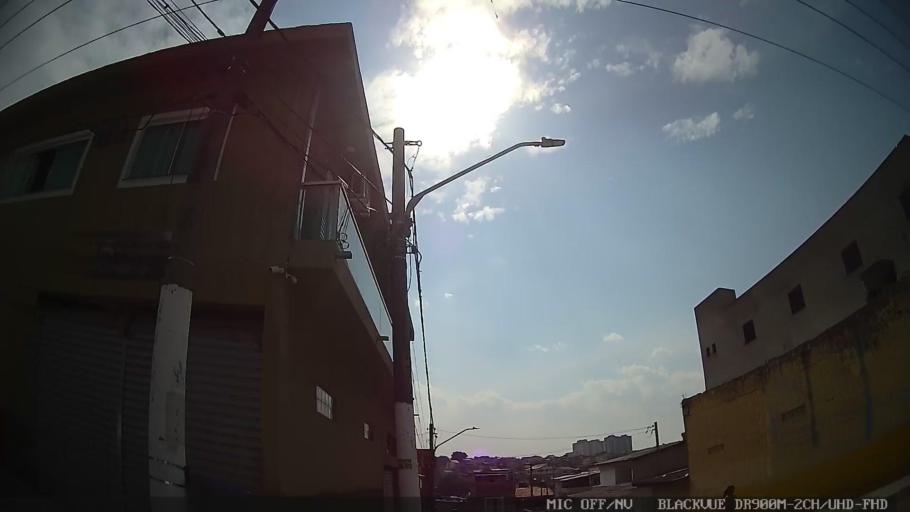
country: BR
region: Sao Paulo
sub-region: Ferraz De Vasconcelos
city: Ferraz de Vasconcelos
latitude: -23.5052
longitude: -46.4153
